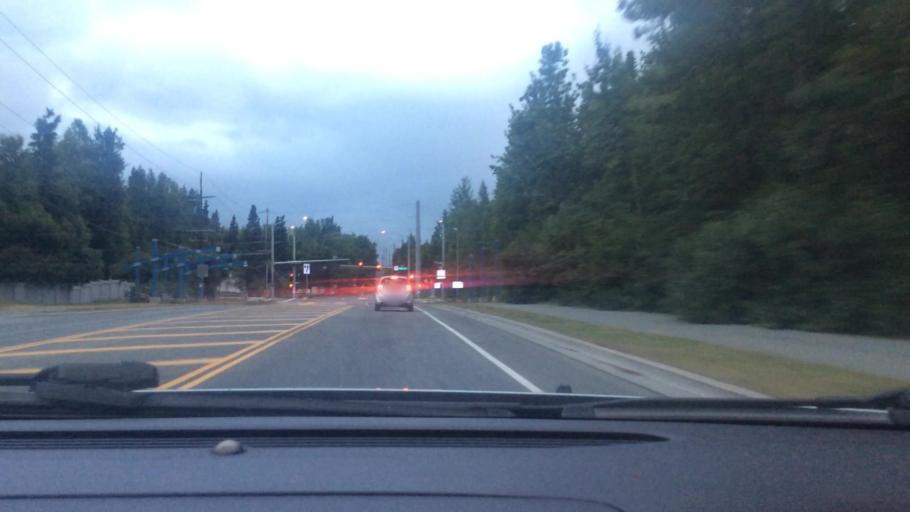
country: US
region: Alaska
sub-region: Anchorage Municipality
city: Anchorage
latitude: 61.1390
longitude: -149.8042
